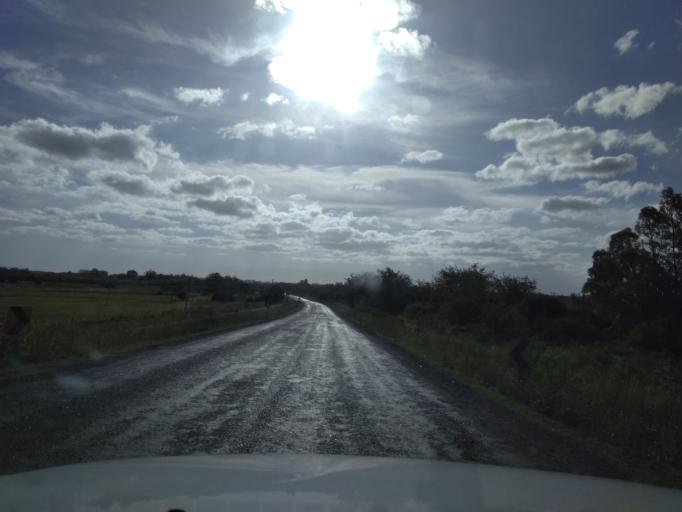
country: UY
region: Canelones
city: San Ramon
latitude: -34.2672
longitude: -55.9310
